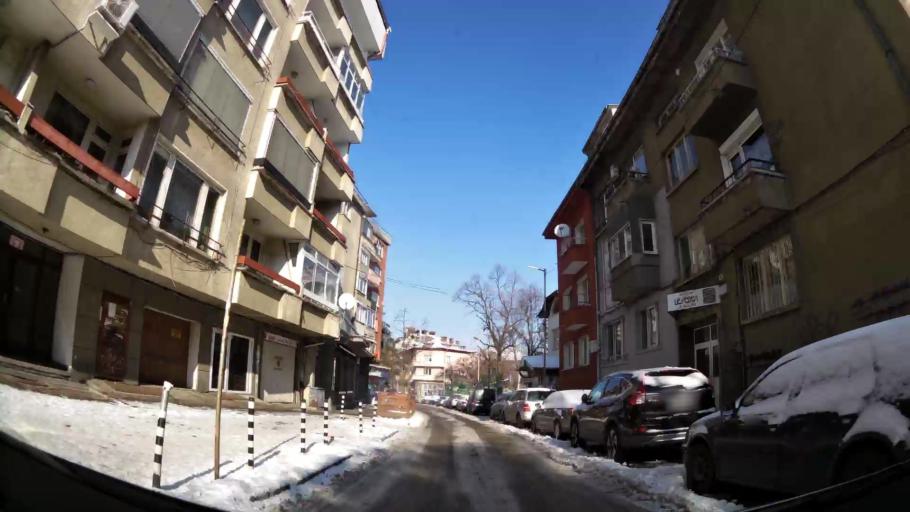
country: BG
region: Sofia-Capital
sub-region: Stolichna Obshtina
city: Sofia
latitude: 42.6819
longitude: 23.3282
